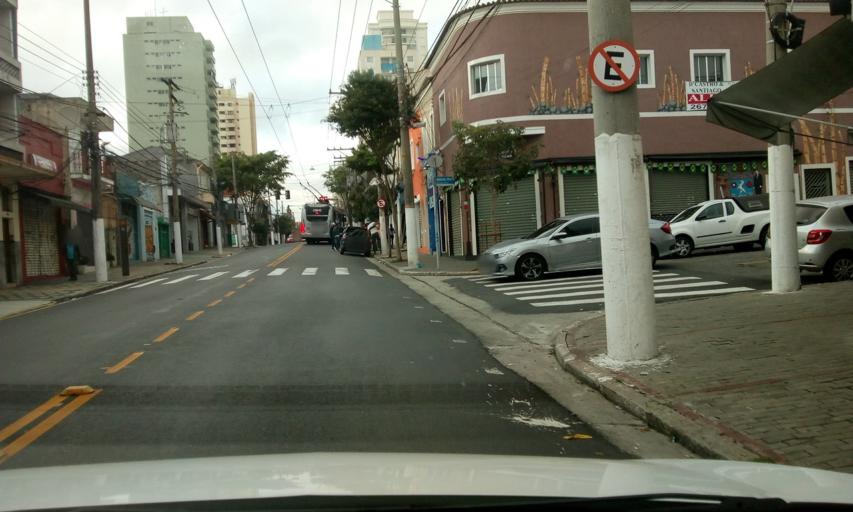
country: BR
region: Sao Paulo
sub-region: Sao Paulo
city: Sao Paulo
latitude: -23.5568
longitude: -46.5940
